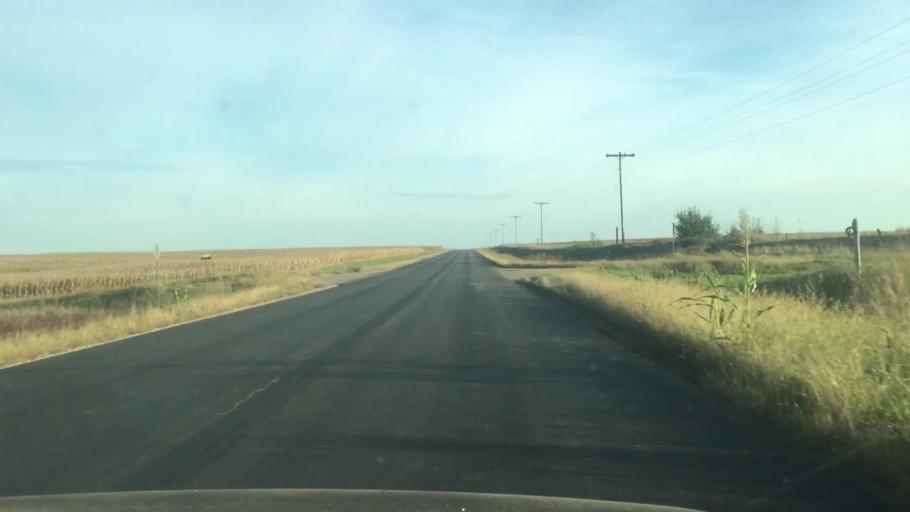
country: US
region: Kansas
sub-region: Marshall County
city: Marysville
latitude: 39.9141
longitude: -96.6009
